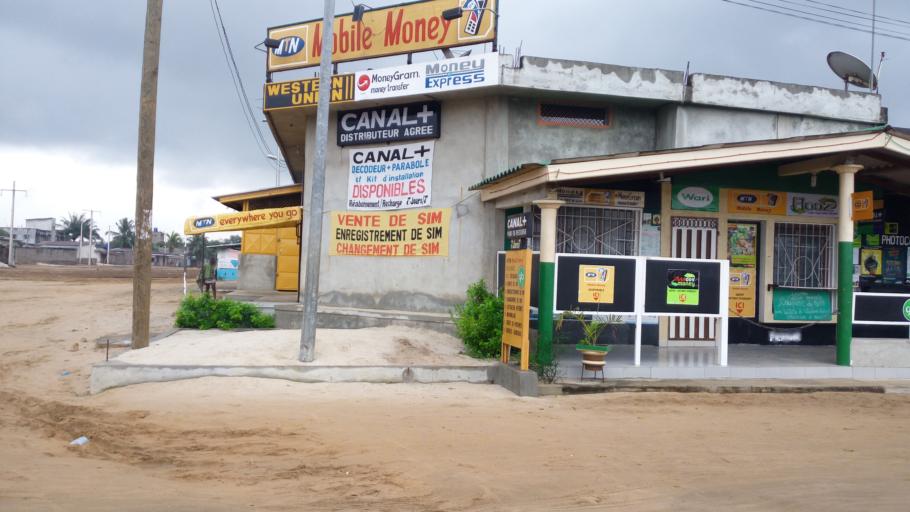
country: BJ
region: Atlantique
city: Hevie
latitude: 6.3903
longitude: 2.2874
